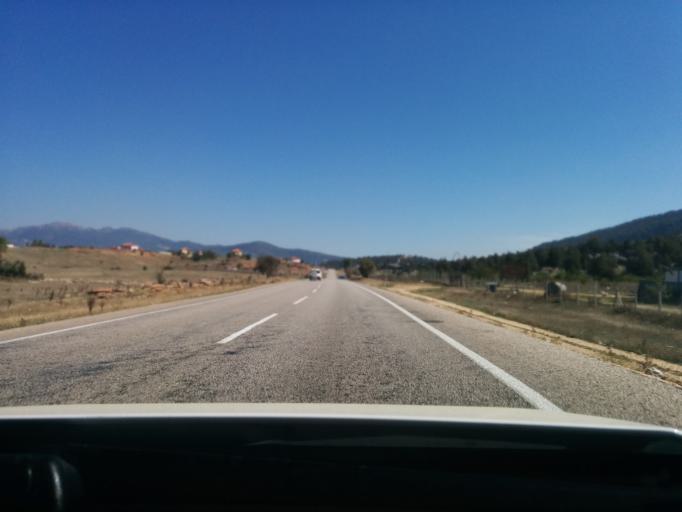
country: TR
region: Mugla
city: Seki
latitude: 36.8152
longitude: 29.5281
